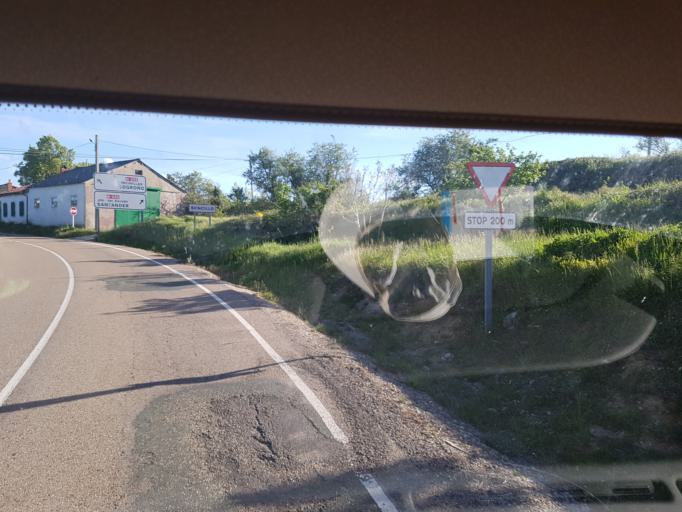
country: ES
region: Cantabria
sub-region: Provincia de Cantabria
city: San Pedro del Romeral
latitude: 42.9732
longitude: -3.7889
